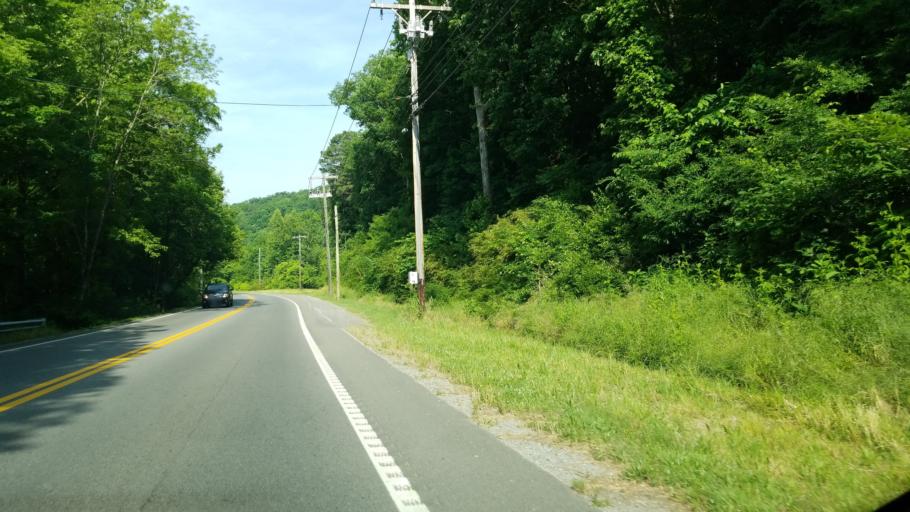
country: US
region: Tennessee
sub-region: Hamilton County
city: Collegedale
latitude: 35.0782
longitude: -85.0372
